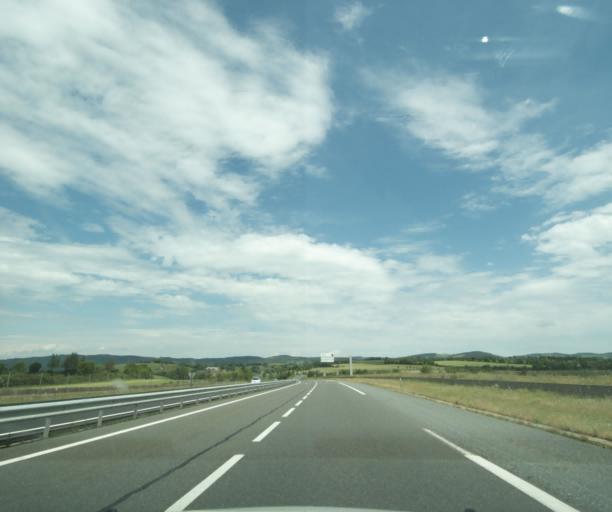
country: FR
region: Midi-Pyrenees
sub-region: Departement de l'Aveyron
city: Severac-le-Chateau
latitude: 44.3035
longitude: 3.1029
